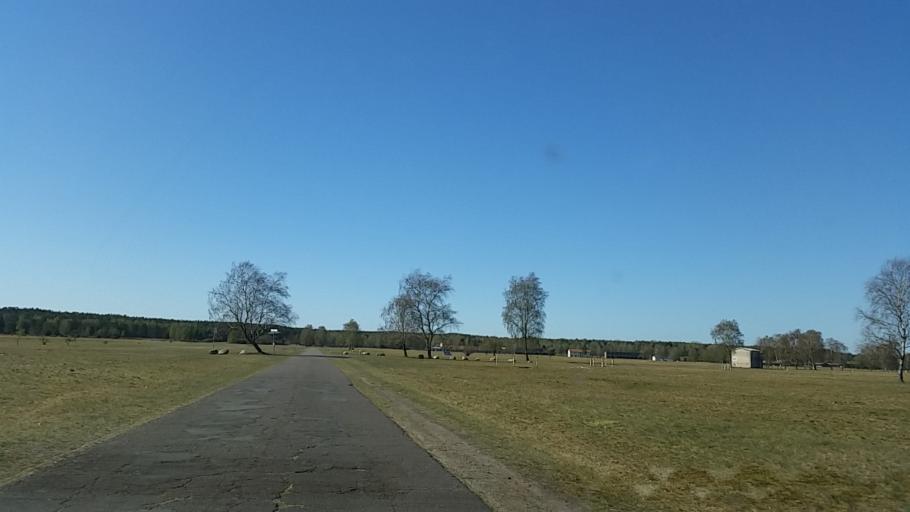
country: DE
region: Lower Saxony
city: Schneverdingen
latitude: 53.1511
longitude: 9.8287
